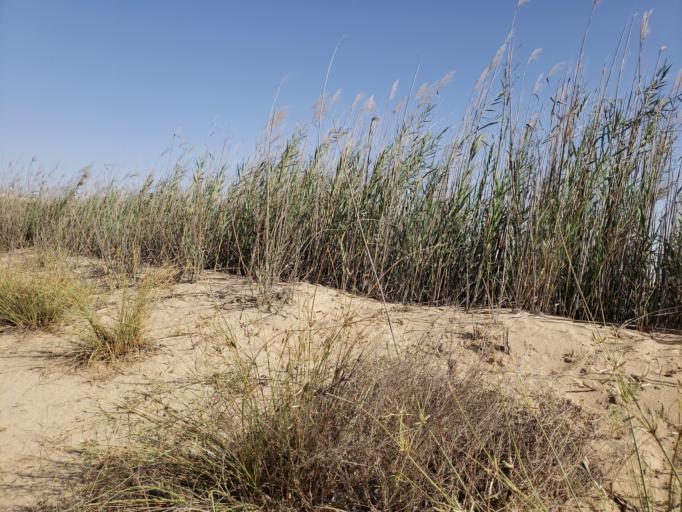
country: AE
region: Dubai
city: Dubai
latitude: 24.9711
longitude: 55.2110
